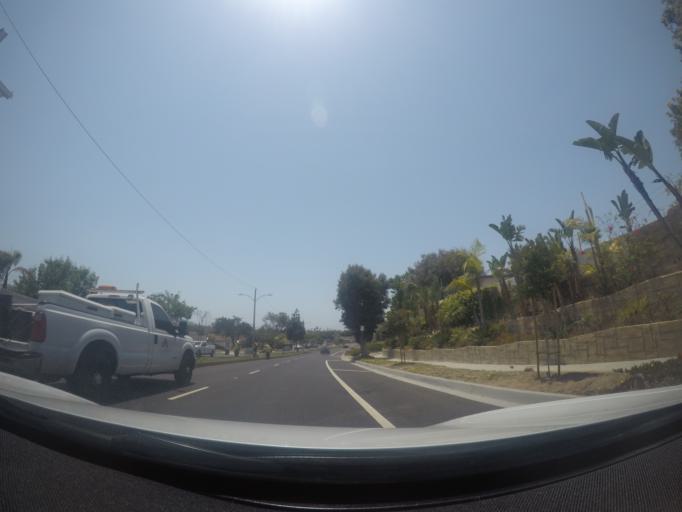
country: US
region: California
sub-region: Los Angeles County
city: Palos Verdes Estates
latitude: 33.8233
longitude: -118.3717
